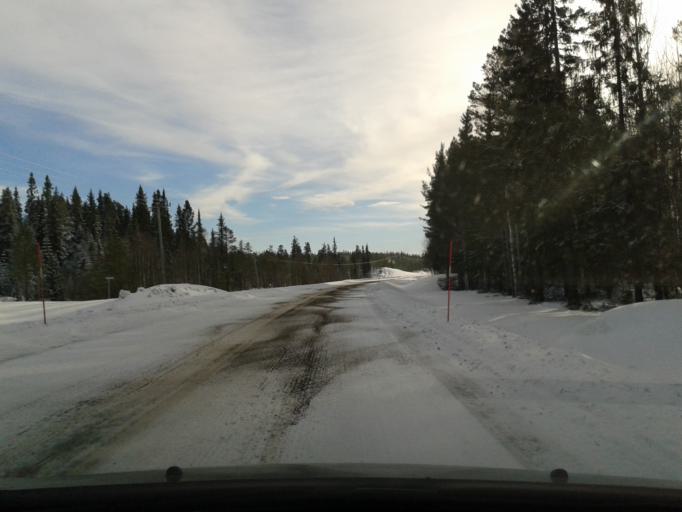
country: SE
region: Vaesterbotten
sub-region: Vilhelmina Kommun
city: Vilhelmina
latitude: 64.5231
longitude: 16.7642
